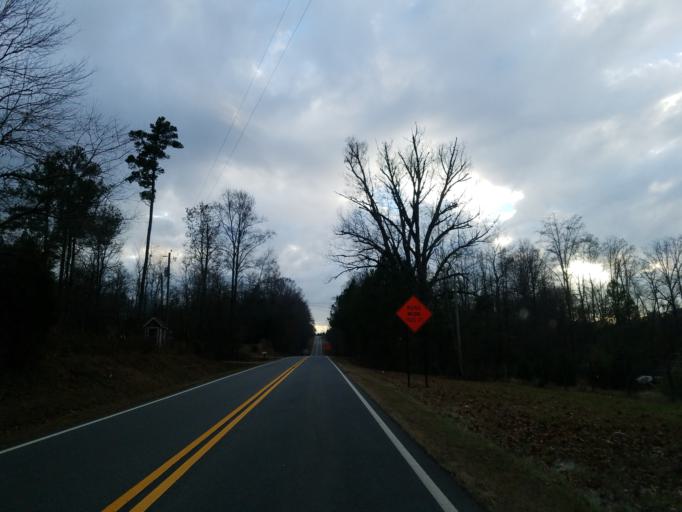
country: US
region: Georgia
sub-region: Dawson County
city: Dawsonville
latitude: 34.3311
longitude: -84.0686
